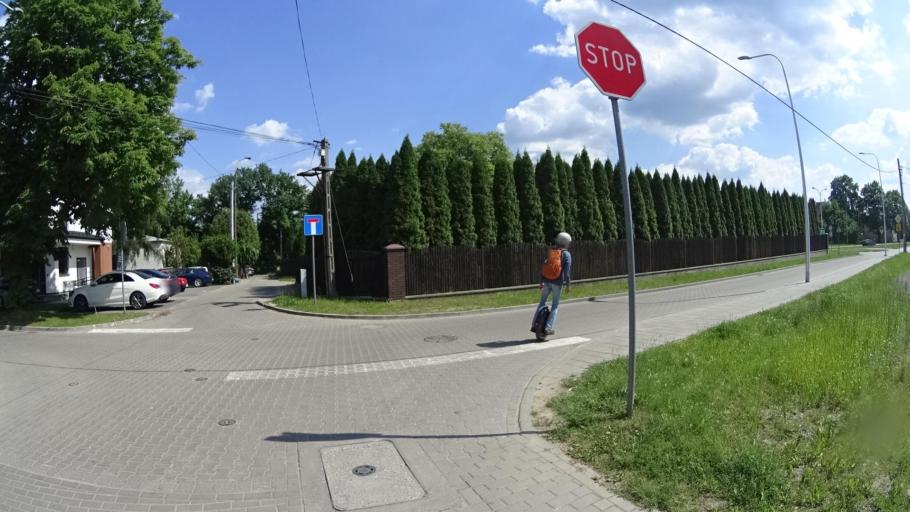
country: PL
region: Masovian Voivodeship
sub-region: Powiat piaseczynski
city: Konstancin-Jeziorna
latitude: 52.0918
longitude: 21.1120
